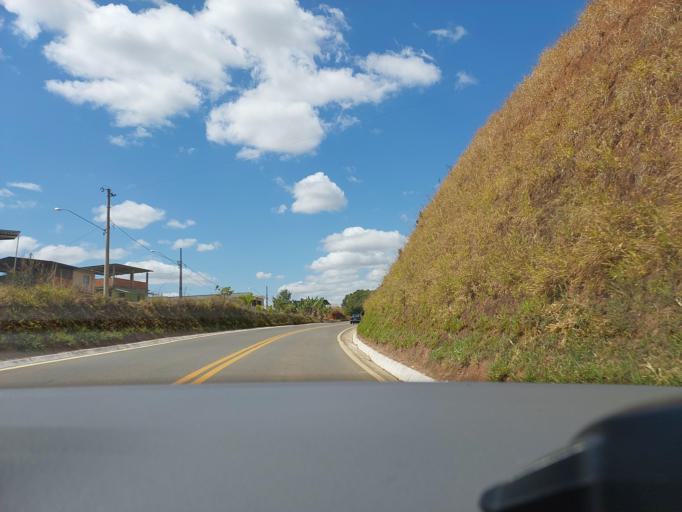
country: BR
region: Minas Gerais
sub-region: Muriae
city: Muriae
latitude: -21.1099
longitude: -42.4503
